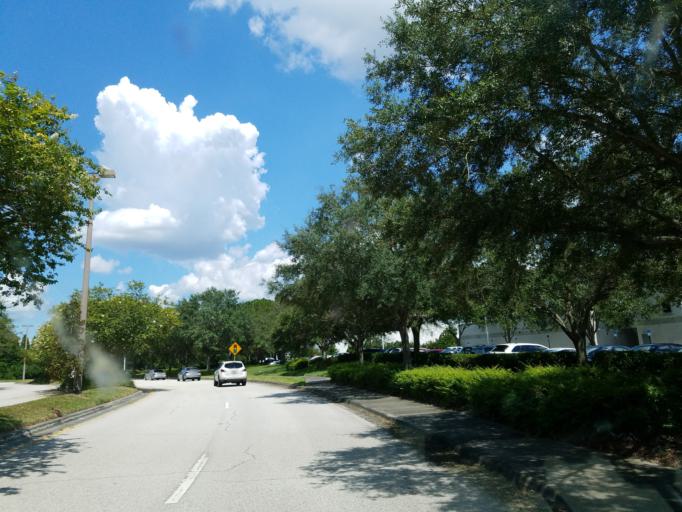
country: US
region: Florida
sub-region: Hillsborough County
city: Progress Village
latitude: 27.9121
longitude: -82.3452
